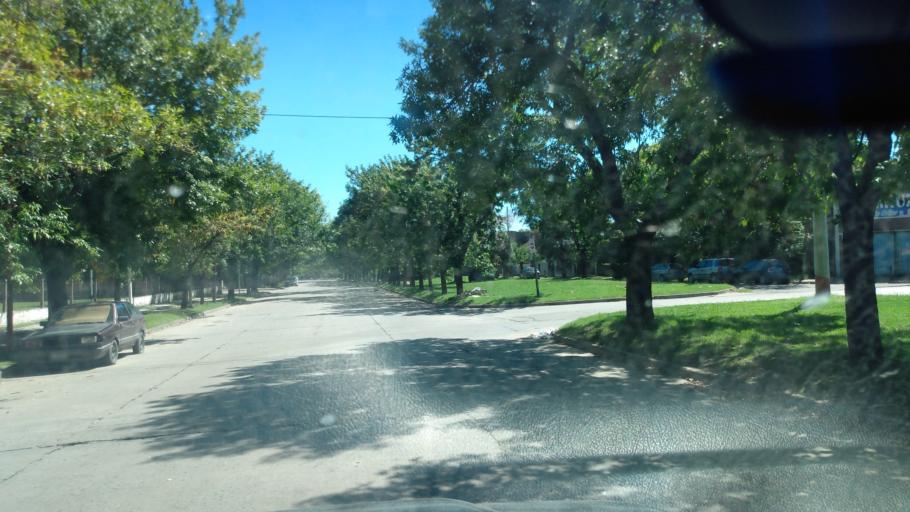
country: AR
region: Buenos Aires
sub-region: Partido de Lujan
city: Lujan
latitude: -34.5770
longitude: -59.1079
